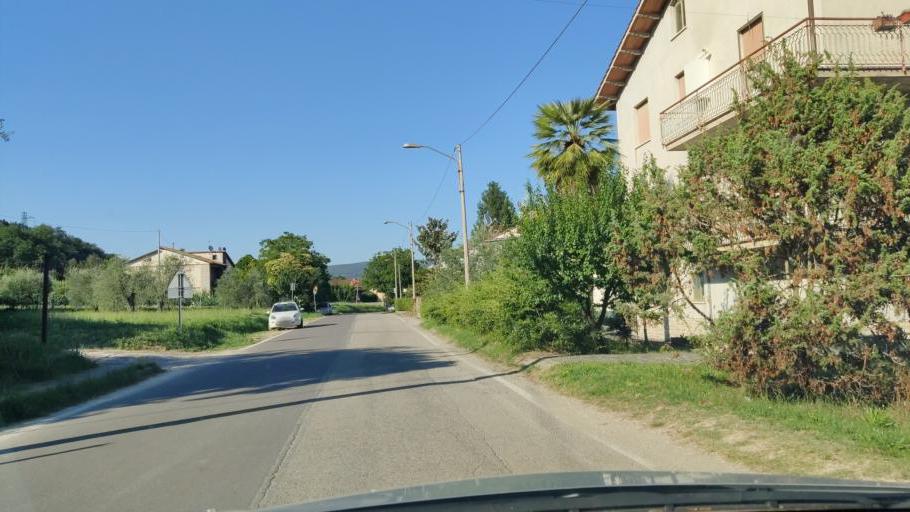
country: IT
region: Latium
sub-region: Provincia di Viterbo
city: Orte Scalo
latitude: 42.4794
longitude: 12.4388
